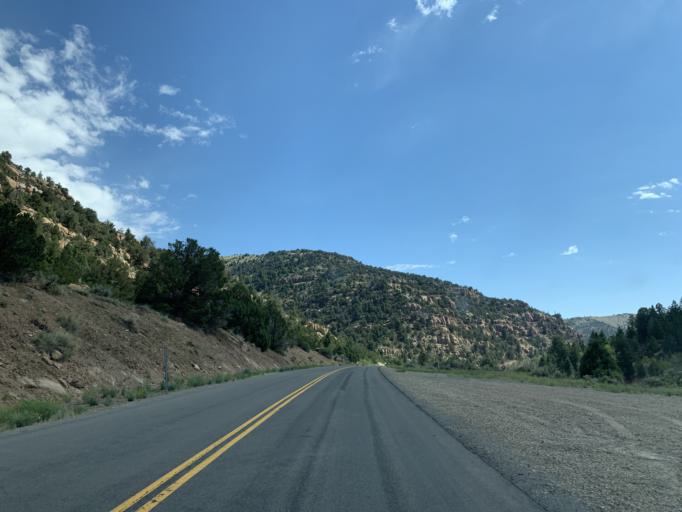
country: US
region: Utah
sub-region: Carbon County
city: East Carbon City
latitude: 39.7515
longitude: -110.5468
